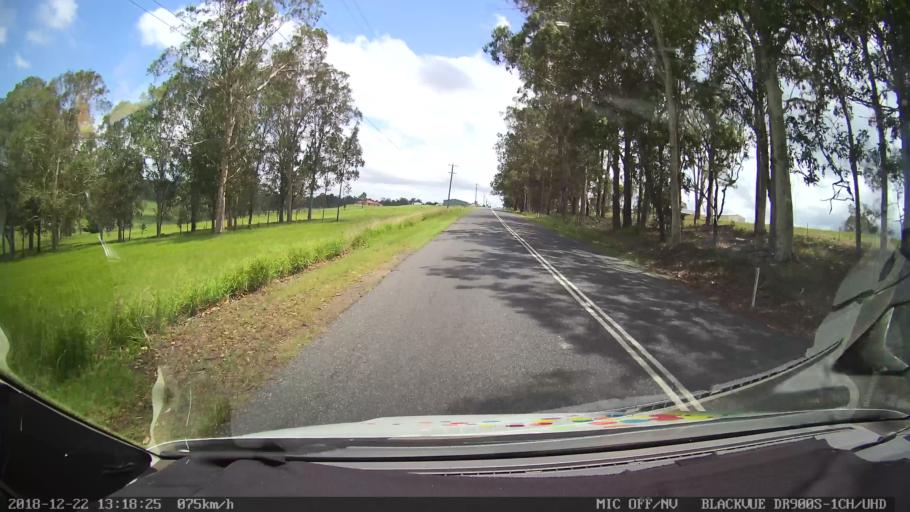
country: AU
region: New South Wales
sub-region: Clarence Valley
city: South Grafton
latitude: -29.7465
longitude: 152.9348
